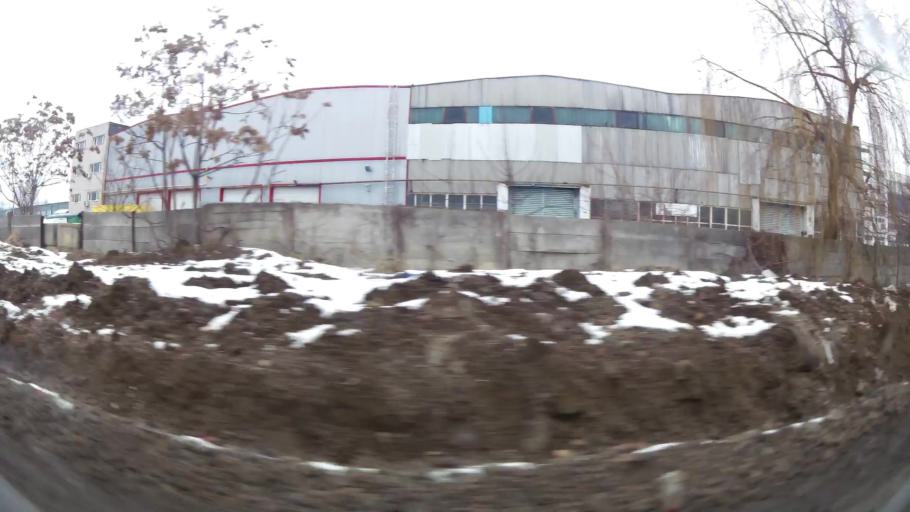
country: RO
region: Ilfov
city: Dobroesti
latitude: 44.4210
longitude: 26.1891
